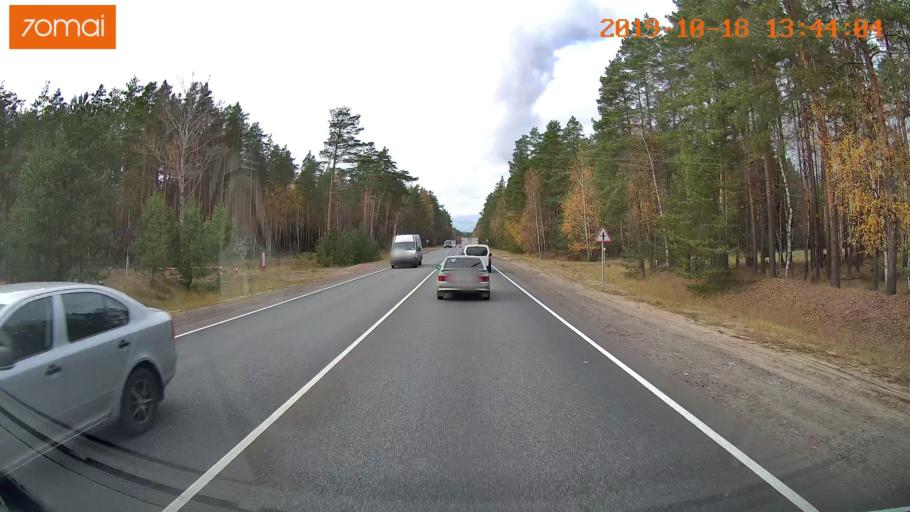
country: RU
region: Rjazan
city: Solotcha
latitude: 54.9344
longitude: 39.9681
